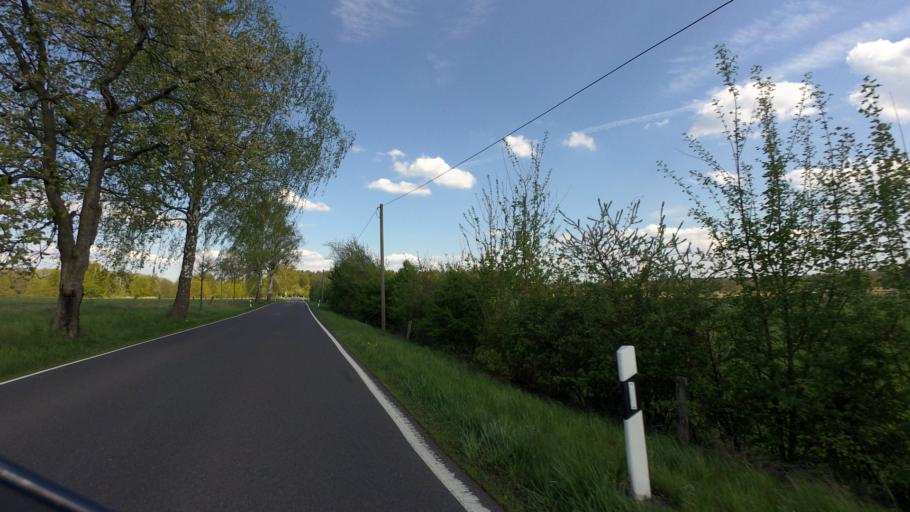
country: DE
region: Brandenburg
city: Templin
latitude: 53.0543
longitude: 13.5592
